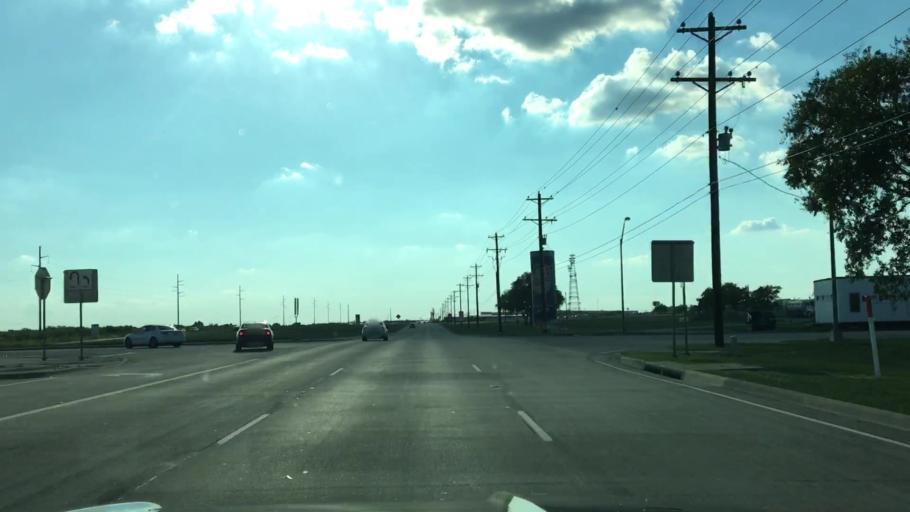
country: US
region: Texas
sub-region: Denton County
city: Justin
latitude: 33.0270
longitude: -97.2874
